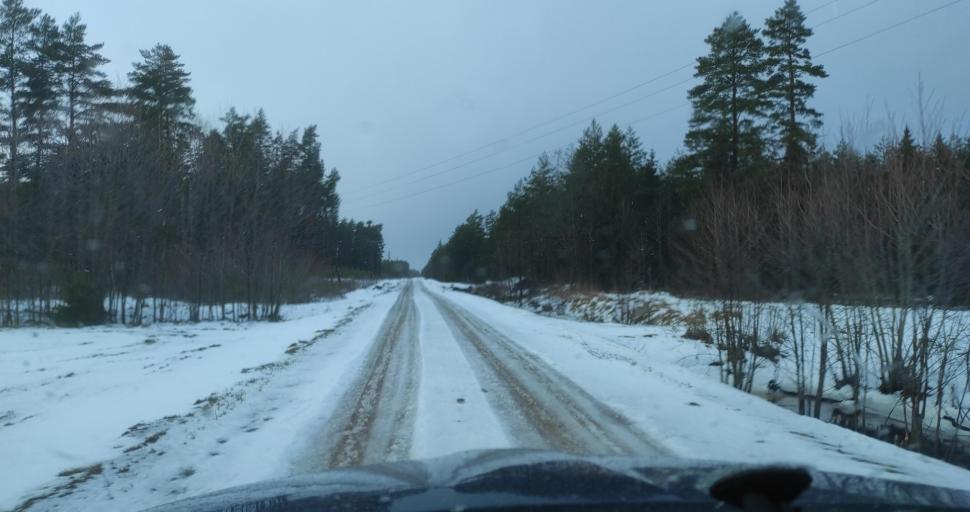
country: LV
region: Dundaga
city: Dundaga
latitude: 57.3798
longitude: 22.1588
